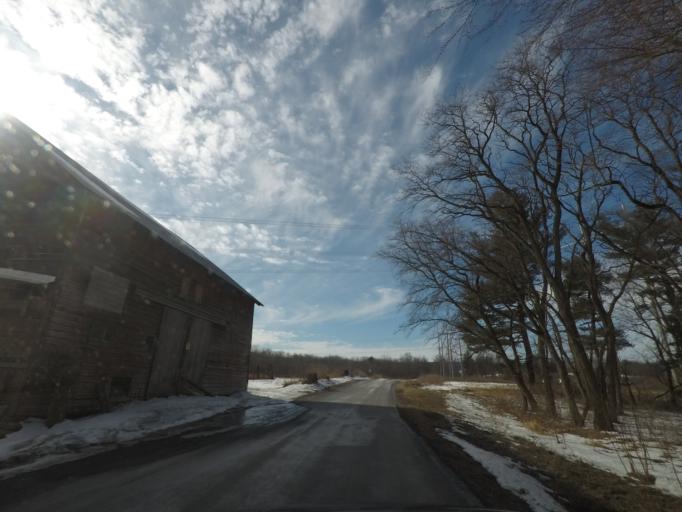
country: US
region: New York
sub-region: Albany County
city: Voorheesville
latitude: 42.6587
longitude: -73.9596
